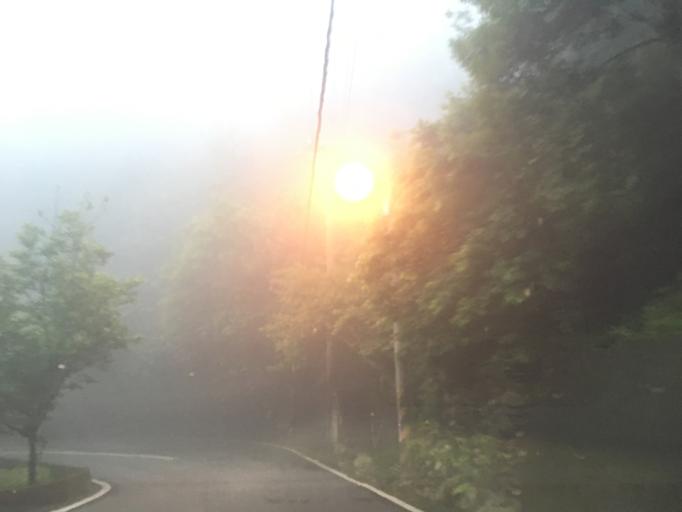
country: TW
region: Taiwan
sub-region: Miaoli
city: Miaoli
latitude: 24.4474
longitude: 120.7906
